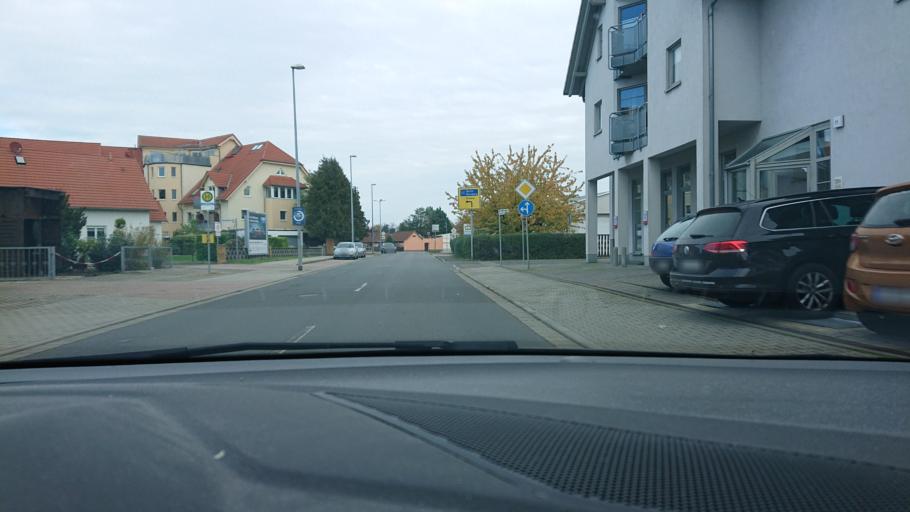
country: DE
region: Saxony
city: Delitzsch
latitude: 51.5206
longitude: 12.3214
